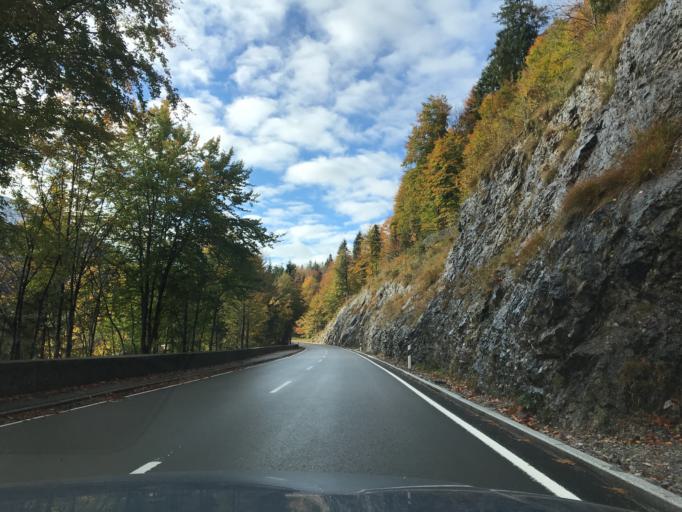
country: DE
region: Bavaria
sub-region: Upper Bavaria
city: Lenggries
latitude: 47.5839
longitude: 11.5474
